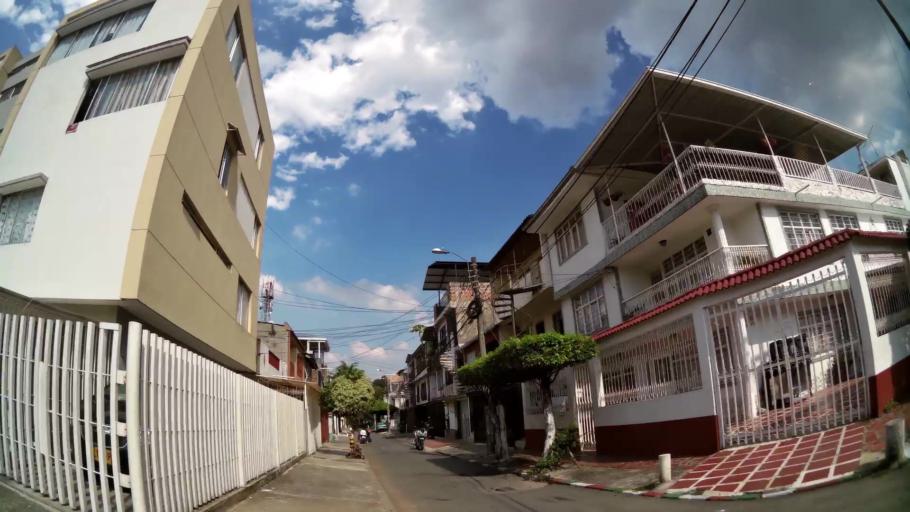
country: CO
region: Valle del Cauca
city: Cali
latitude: 3.4154
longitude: -76.5163
